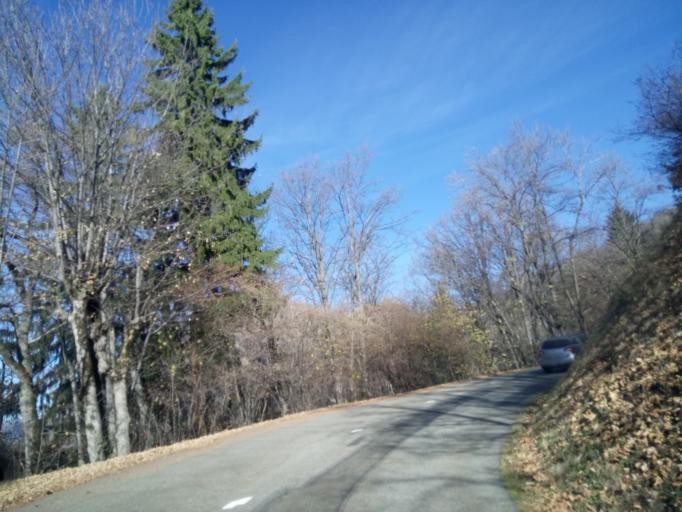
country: FR
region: Rhone-Alpes
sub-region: Departement de la Savoie
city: Saint-Michel-de-Maurienne
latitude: 45.2286
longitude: 6.4824
